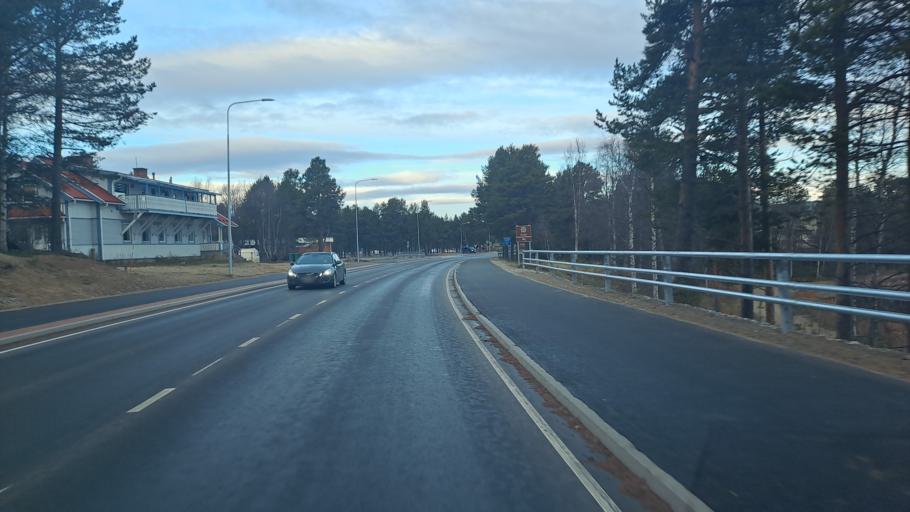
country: FI
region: Lapland
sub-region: Pohjois-Lappi
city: Inari
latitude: 68.9063
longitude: 27.0200
